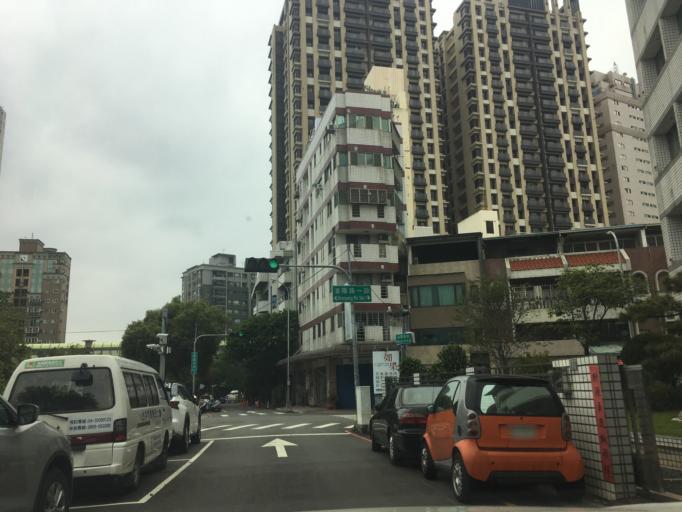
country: TW
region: Taiwan
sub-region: Taichung City
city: Taichung
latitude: 24.1755
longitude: 120.6743
